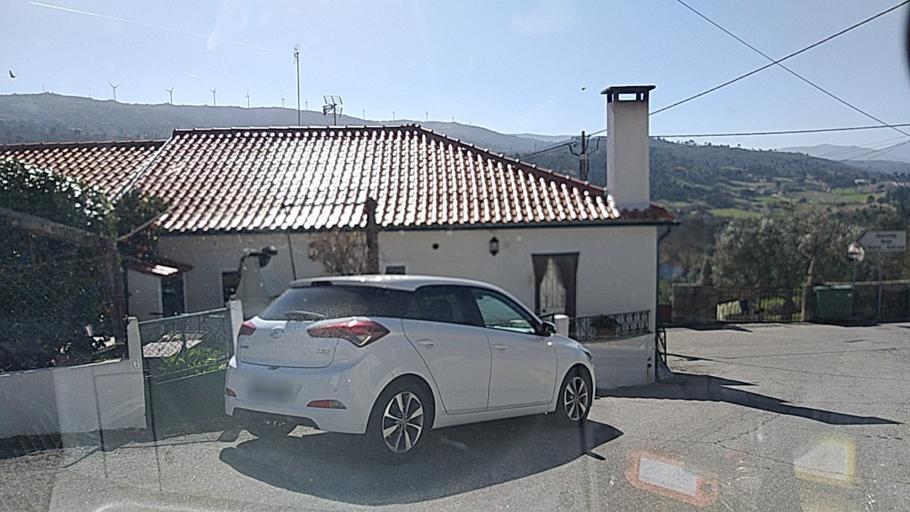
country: PT
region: Guarda
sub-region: Celorico da Beira
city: Celorico da Beira
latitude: 40.6198
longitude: -7.4080
